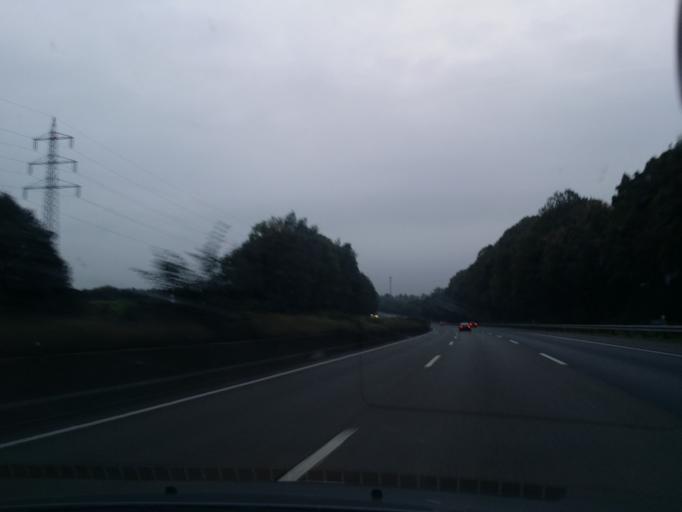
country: DE
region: North Rhine-Westphalia
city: Burscheid
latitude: 51.0690
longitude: 7.0840
